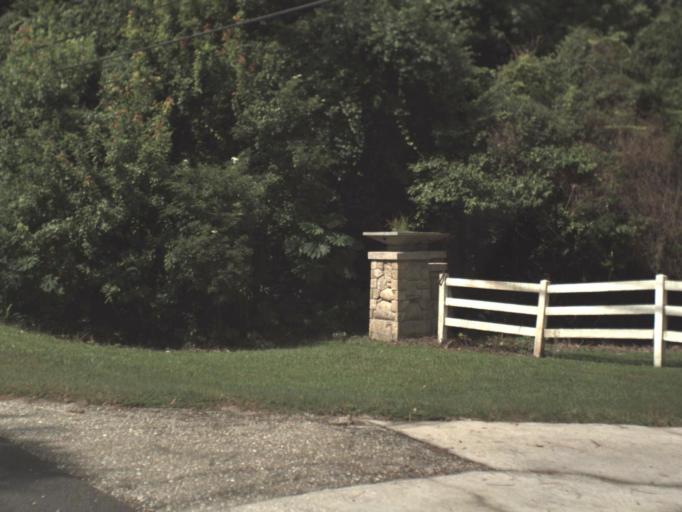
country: US
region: Florida
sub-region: Clay County
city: Green Cove Springs
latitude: 30.0530
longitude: -81.6673
